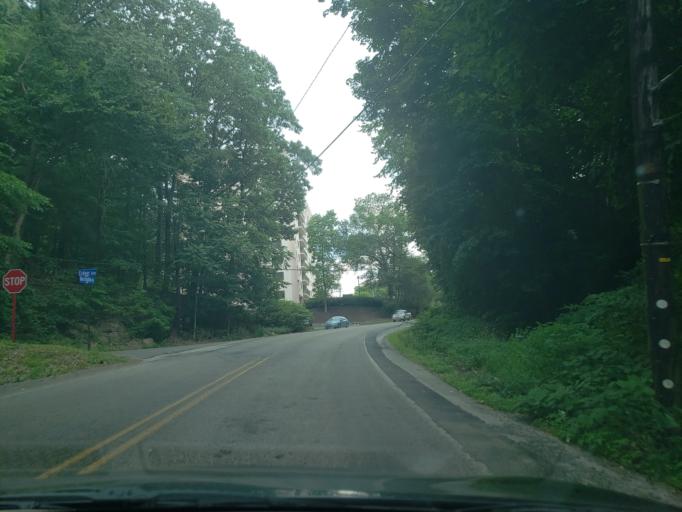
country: US
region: Pennsylvania
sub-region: Allegheny County
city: Avalon
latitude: 40.5017
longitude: -80.0633
